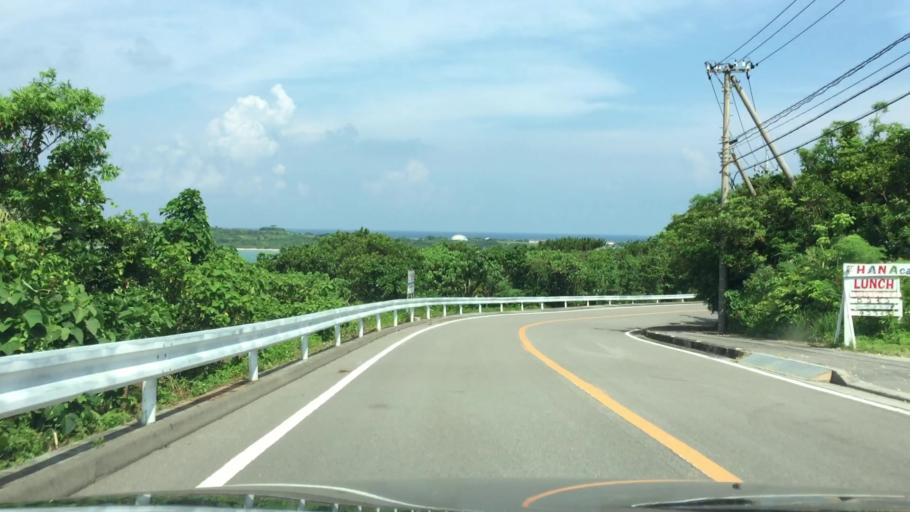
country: JP
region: Okinawa
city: Ishigaki
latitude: 24.5143
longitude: 124.2647
